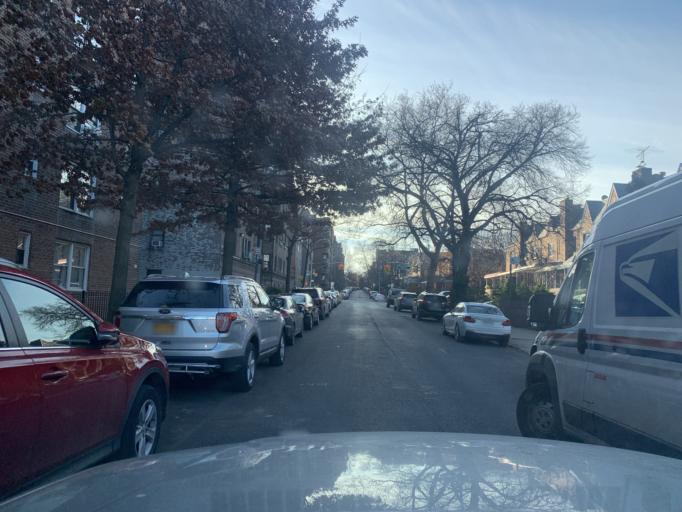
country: US
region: New York
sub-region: Queens County
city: Long Island City
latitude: 40.7539
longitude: -73.8907
